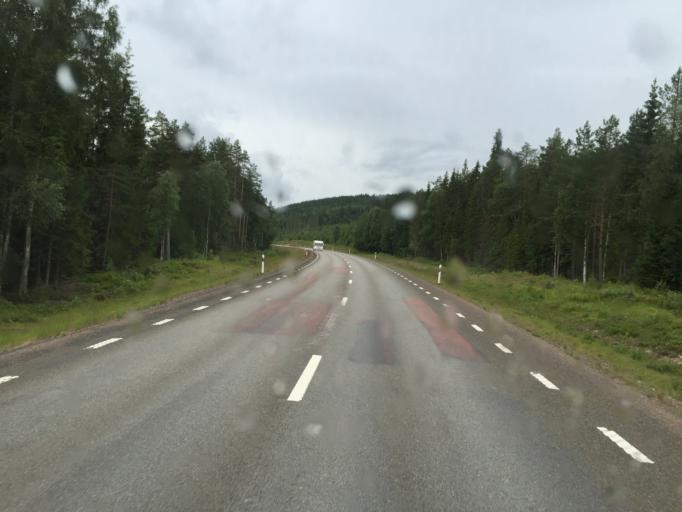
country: SE
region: Dalarna
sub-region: Malung-Saelens kommun
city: Malung
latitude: 60.6395
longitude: 13.6193
